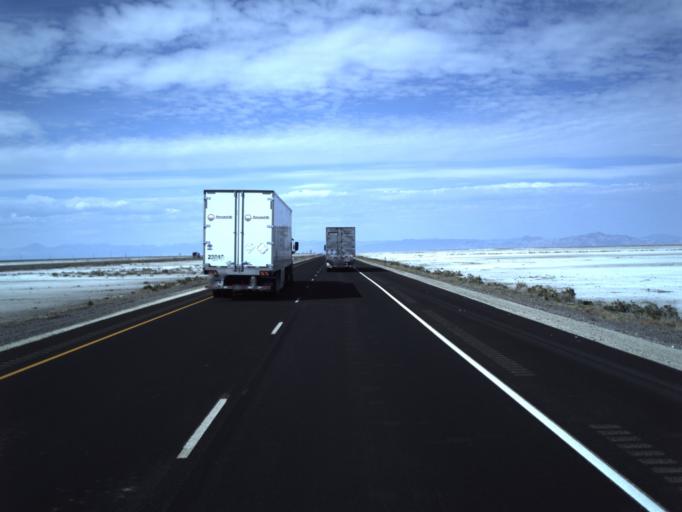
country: US
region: Utah
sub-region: Tooele County
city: Wendover
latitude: 40.7316
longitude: -113.4928
